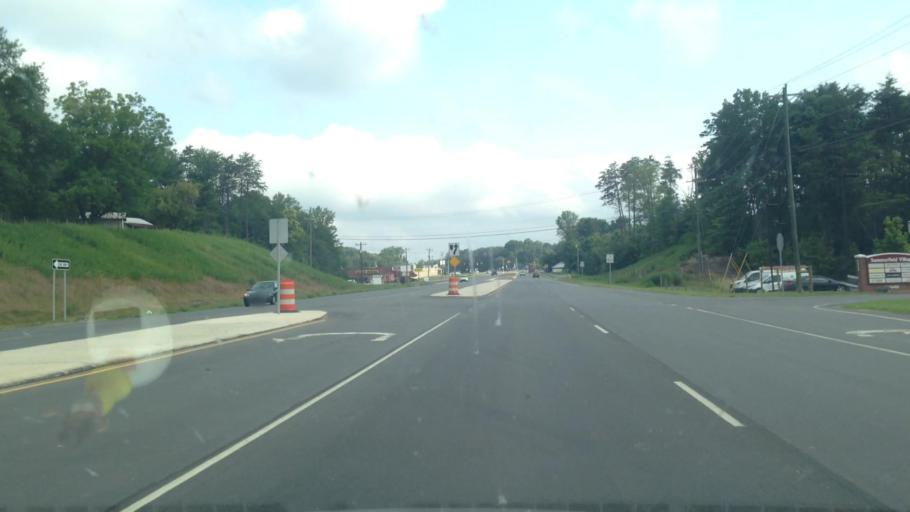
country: US
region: North Carolina
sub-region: Guilford County
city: Summerfield
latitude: 36.1884
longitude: -79.8899
